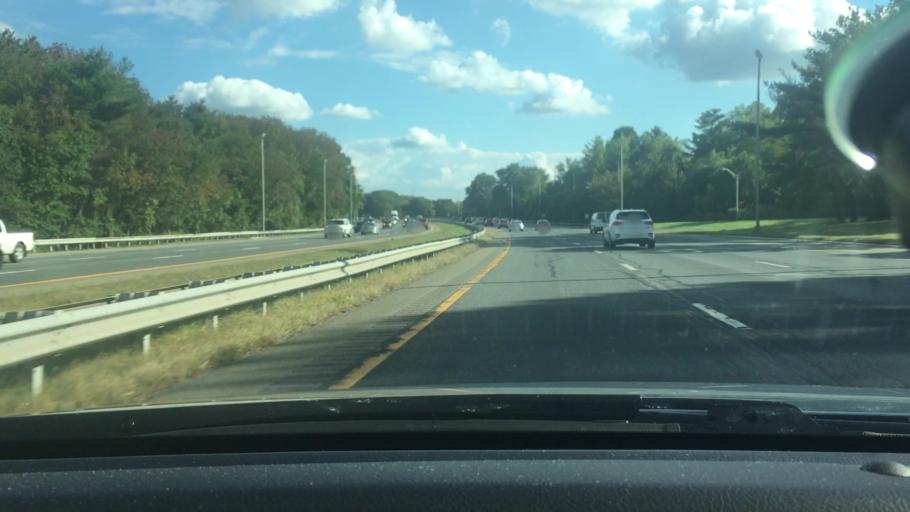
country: US
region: New Jersey
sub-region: Morris County
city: Parsippany
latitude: 40.8757
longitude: -74.4207
